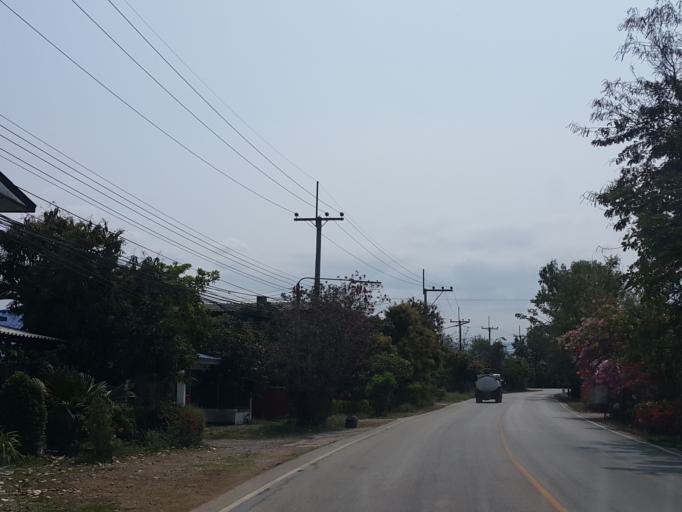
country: TH
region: Lamphun
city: Ban Thi
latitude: 18.6590
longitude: 99.1113
